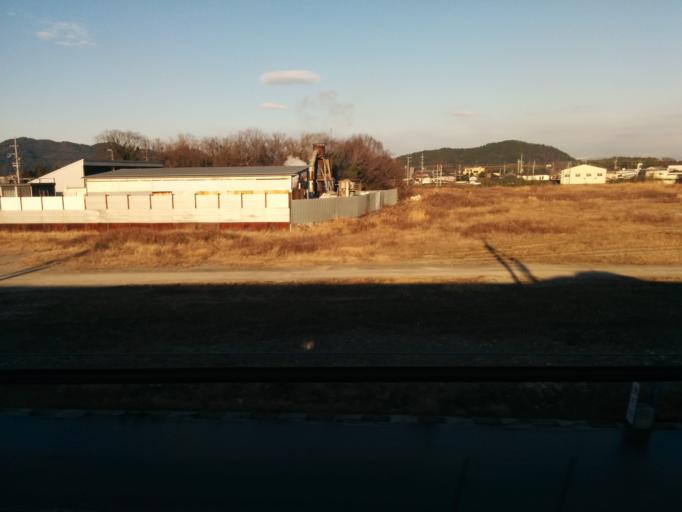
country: JP
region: Shiga Prefecture
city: Youkaichi
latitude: 35.1630
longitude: 136.2039
